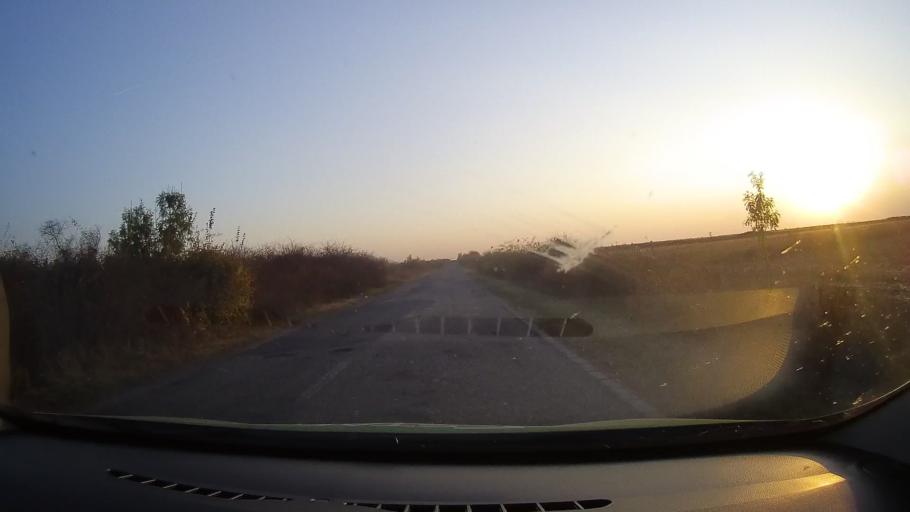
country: RO
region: Arad
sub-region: Comuna Sicula
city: Sicula
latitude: 46.4106
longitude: 21.7331
